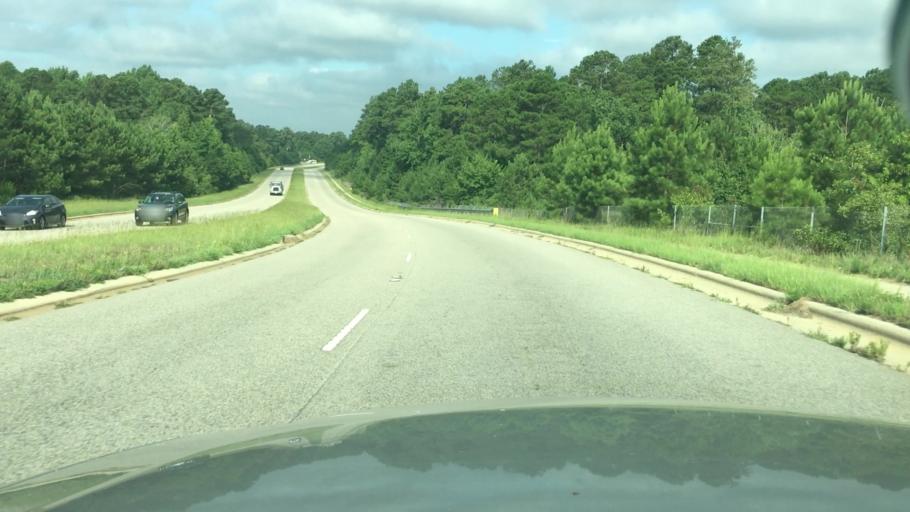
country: US
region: North Carolina
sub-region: Cumberland County
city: Hope Mills
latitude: 34.9921
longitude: -78.9515
